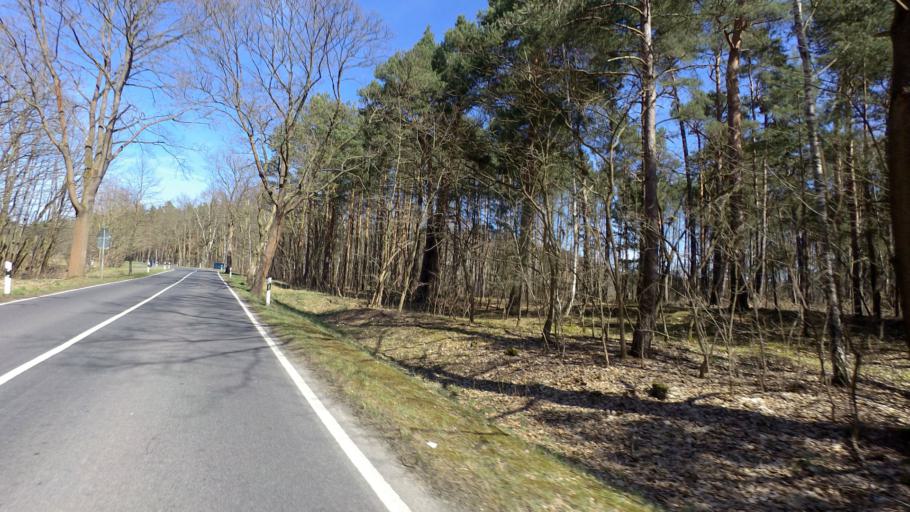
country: DE
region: Brandenburg
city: Storkow
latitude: 52.2003
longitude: 13.9235
